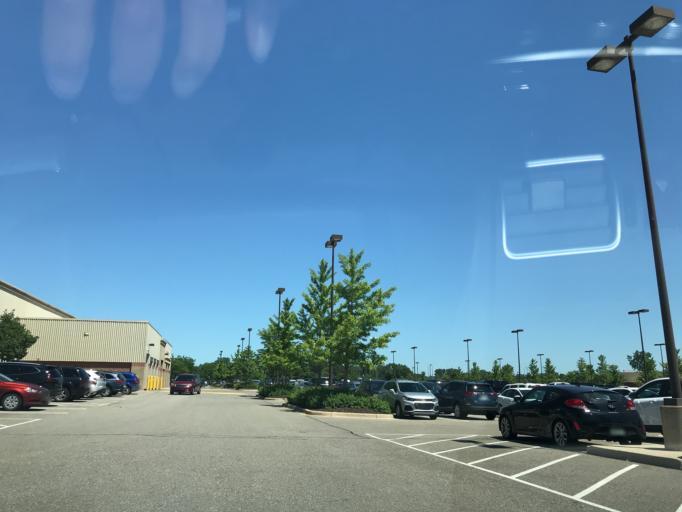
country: US
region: Michigan
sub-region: Livingston County
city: Brighton
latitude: 42.5026
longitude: -83.7615
